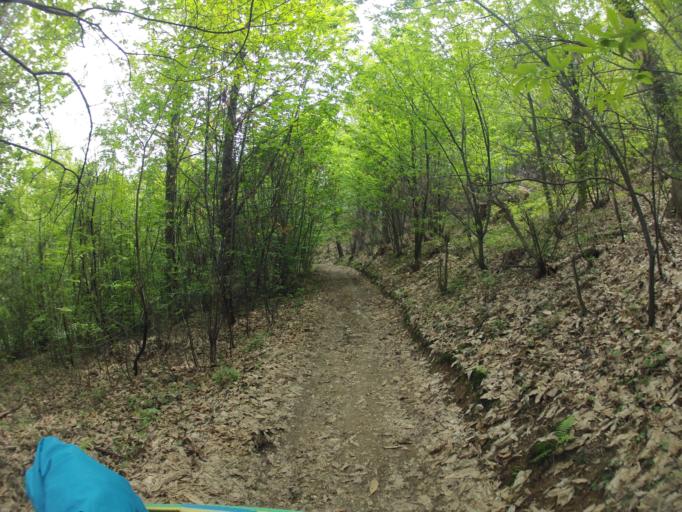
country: IT
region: Piedmont
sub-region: Provincia di Cuneo
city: Peveragno
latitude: 44.3316
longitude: 7.6090
